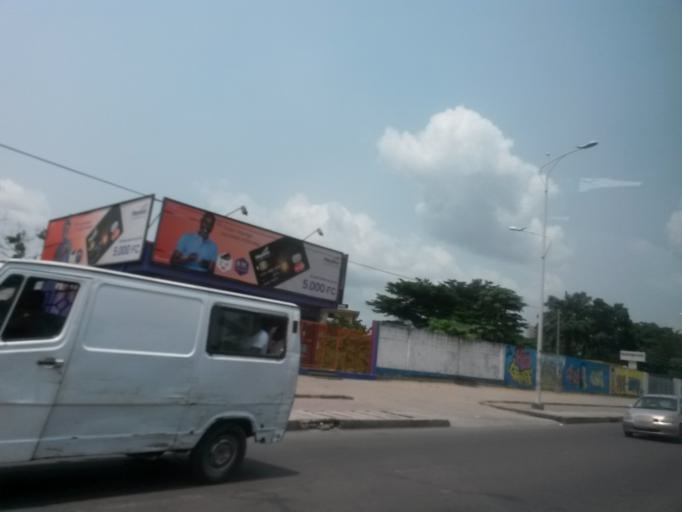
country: CD
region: Kinshasa
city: Kinshasa
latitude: -4.3157
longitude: 15.2916
